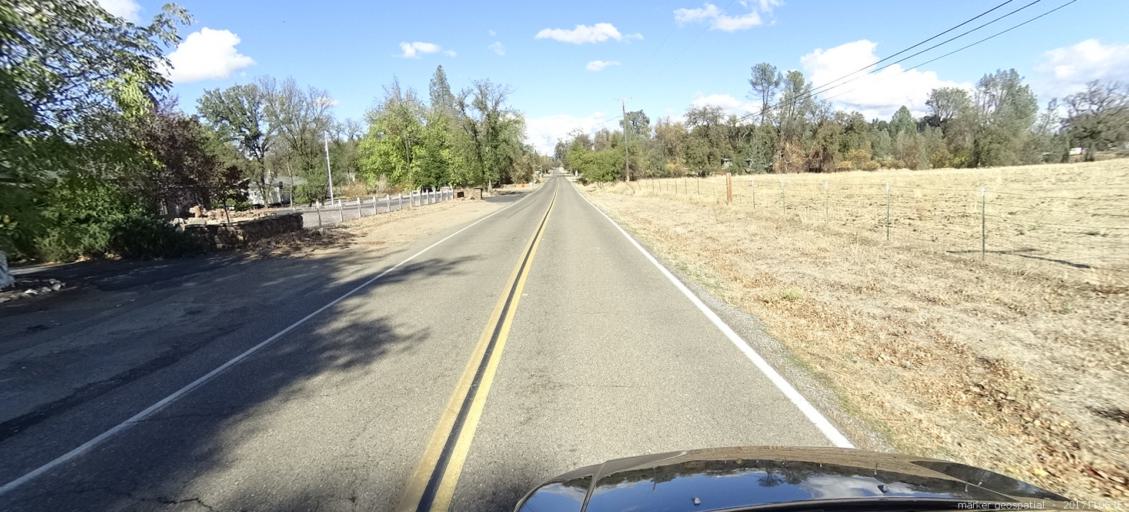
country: US
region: California
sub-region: Shasta County
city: Palo Cedro
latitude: 40.5726
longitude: -122.2199
